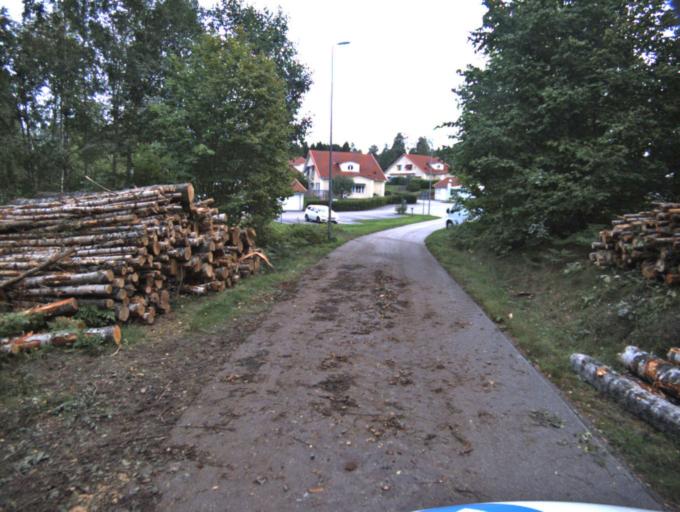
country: SE
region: Vaestra Goetaland
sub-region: Ulricehamns Kommun
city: Ulricehamn
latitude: 57.8053
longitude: 13.4306
